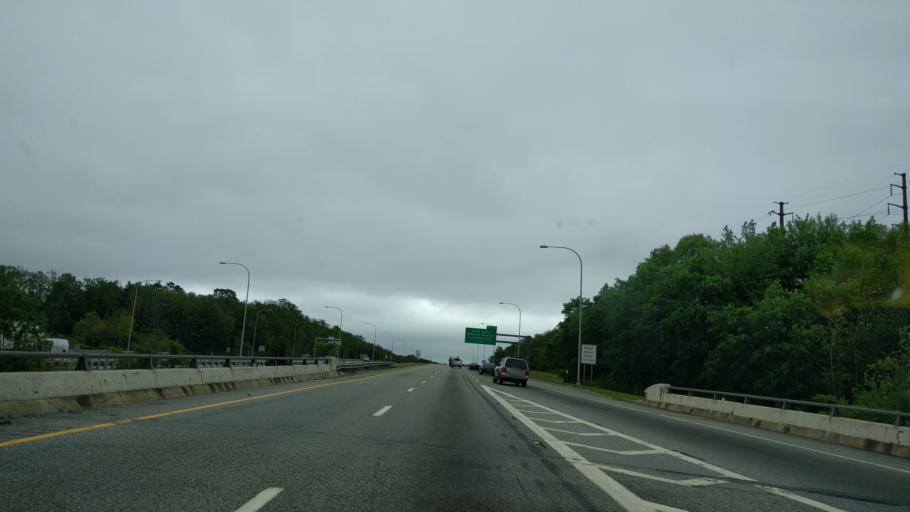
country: US
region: Rhode Island
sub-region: Providence County
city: Johnston
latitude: 41.8199
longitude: -71.5127
